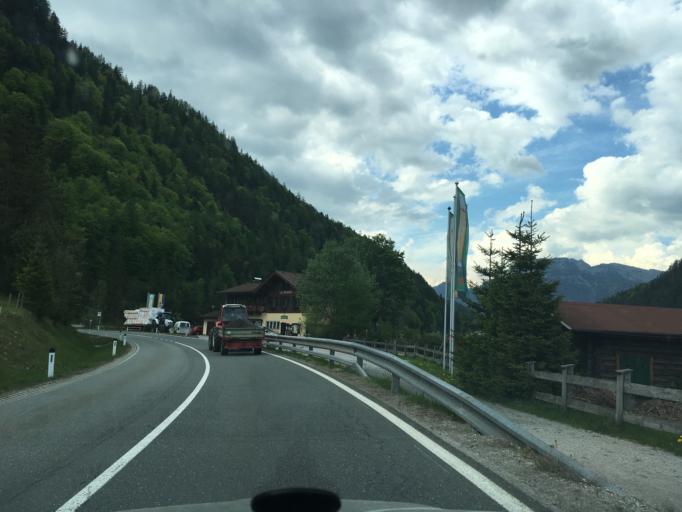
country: AT
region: Tyrol
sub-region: Politischer Bezirk Kitzbuhel
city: Waidring
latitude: 47.5393
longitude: 12.5680
